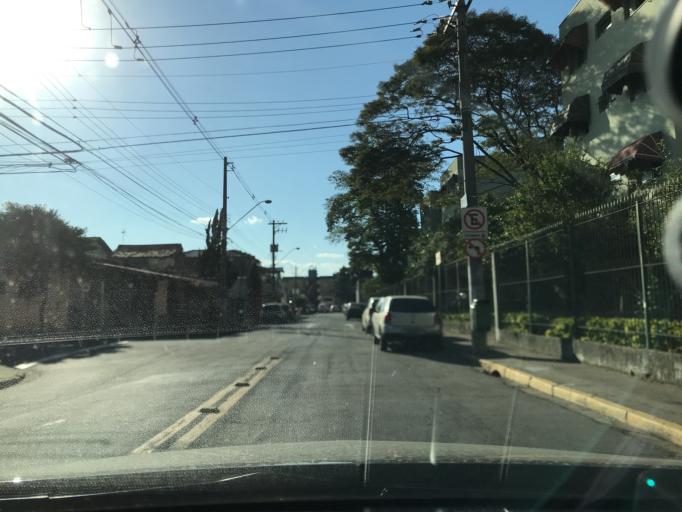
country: BR
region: Sao Paulo
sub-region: Sao Jose Dos Campos
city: Sao Jose dos Campos
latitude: -23.1857
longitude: -45.8596
